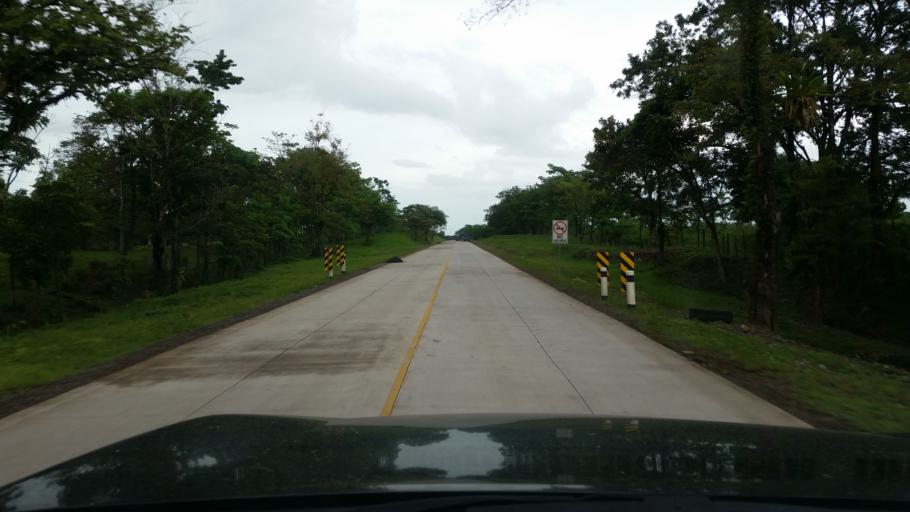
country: NI
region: Matagalpa
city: Rio Blanco
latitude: 13.1402
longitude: -85.0072
